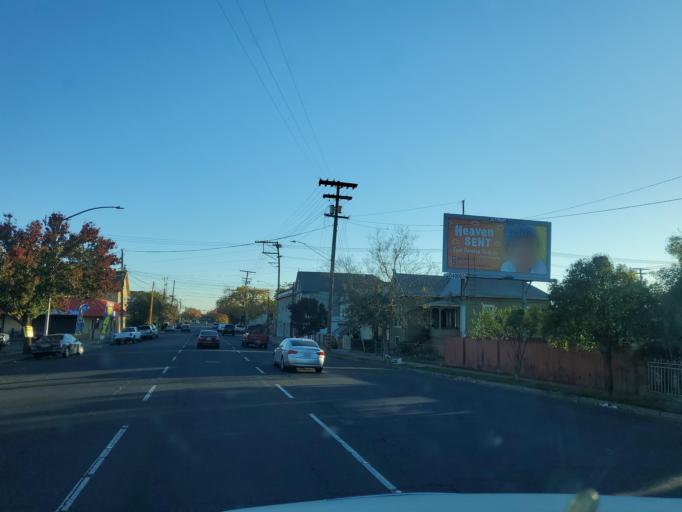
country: US
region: California
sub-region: San Joaquin County
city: Stockton
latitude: 37.9425
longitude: -121.2884
